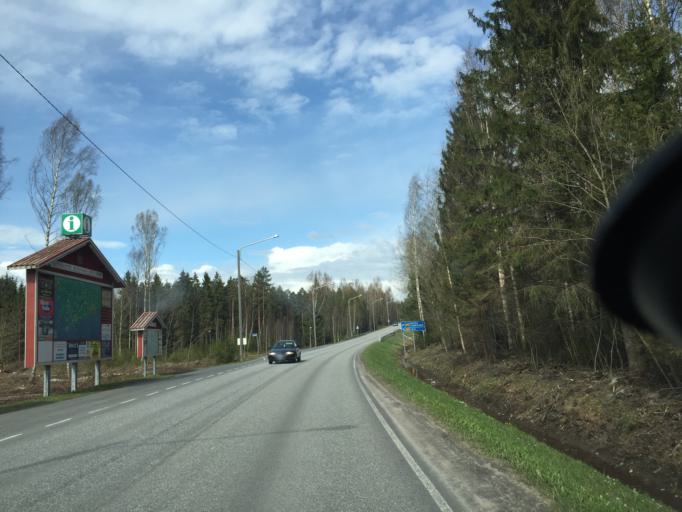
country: FI
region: Uusimaa
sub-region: Raaseporin
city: Ekenaes
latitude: 60.0592
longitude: 23.2984
